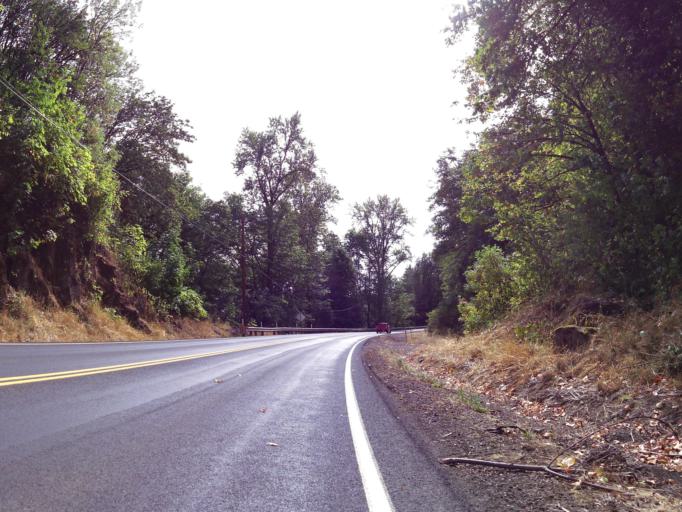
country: US
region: Washington
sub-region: Cowlitz County
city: Castle Rock
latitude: 46.3579
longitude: -122.9337
